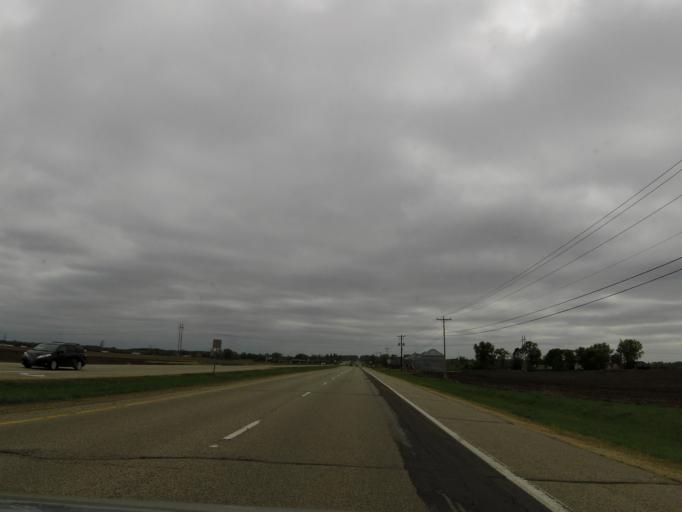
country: US
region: Minnesota
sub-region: Washington County
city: Lake Elmo
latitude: 44.9595
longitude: -92.8629
